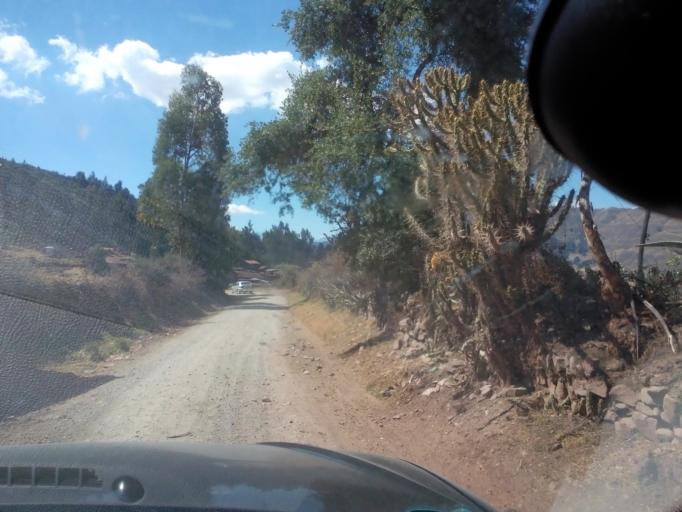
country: PE
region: Cusco
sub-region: Provincia de Anta
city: Zurite
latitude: -13.4385
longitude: -72.2334
